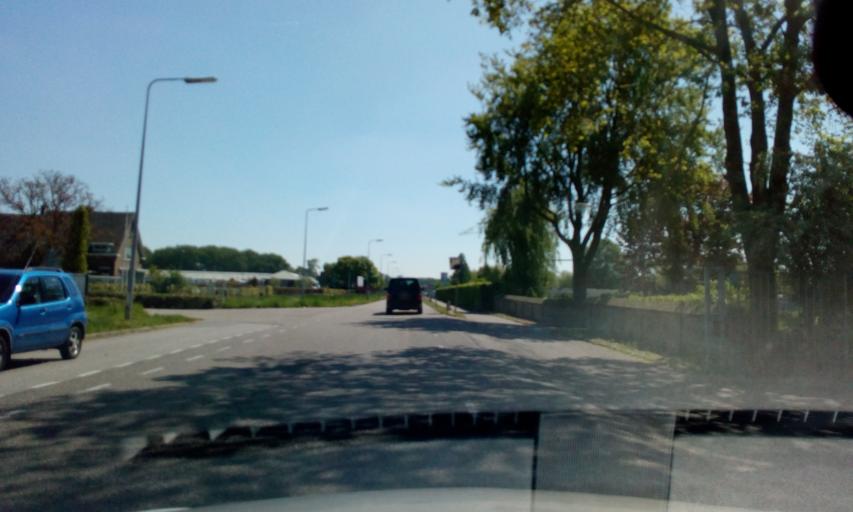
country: NL
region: South Holland
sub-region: Gemeente Zwijndrecht
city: Zwijndrecht
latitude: 51.8356
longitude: 4.6086
